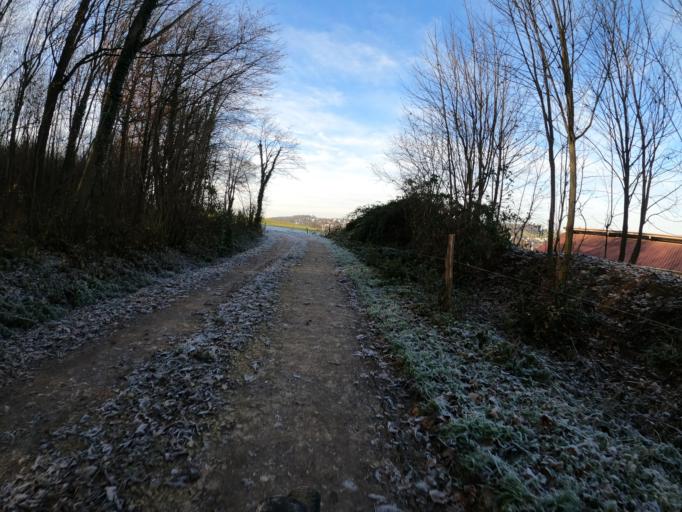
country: DE
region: Baden-Wuerttemberg
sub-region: Regierungsbezirk Stuttgart
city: Goeppingen
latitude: 48.7048
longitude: 9.6309
